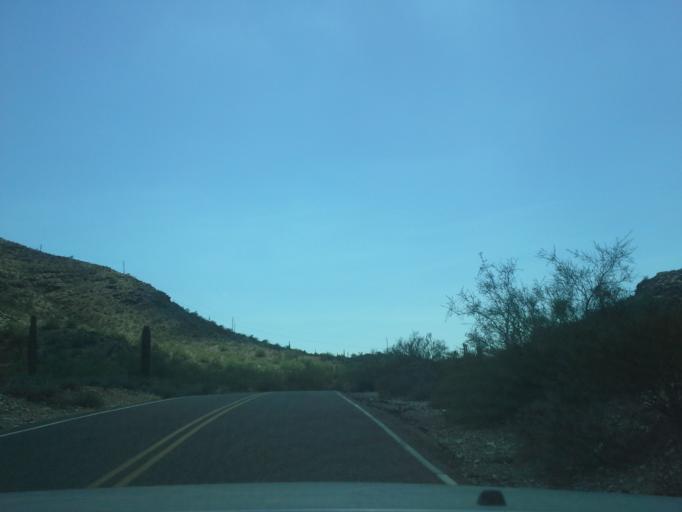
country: US
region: Arizona
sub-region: Maricopa County
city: Laveen
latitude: 33.3377
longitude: -112.0659
